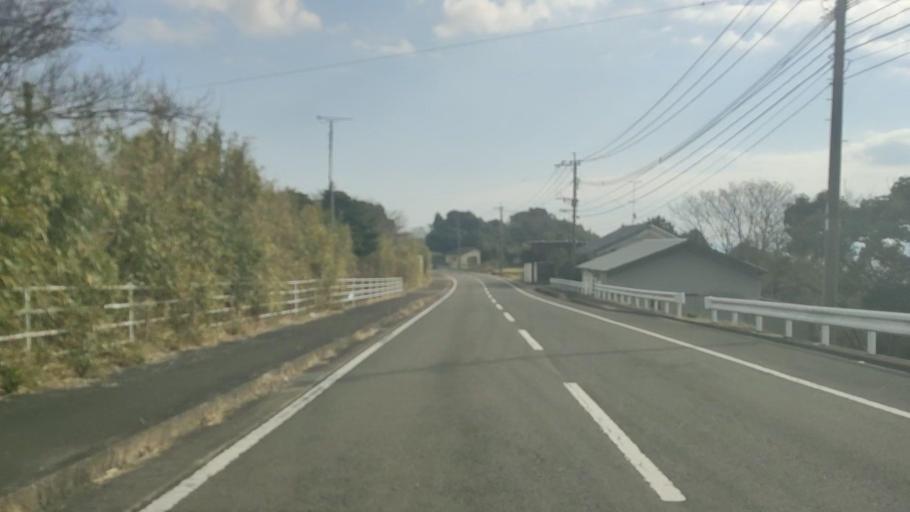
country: JP
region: Nagasaki
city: Shimabara
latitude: 32.6808
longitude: 130.2764
